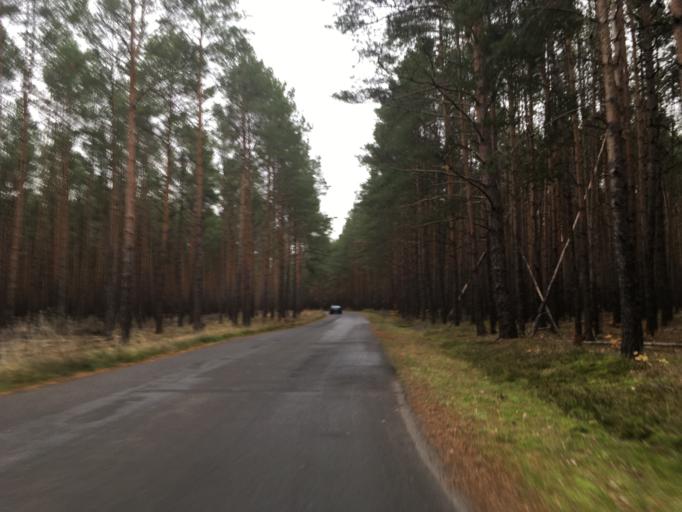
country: DE
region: Brandenburg
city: Mullrose
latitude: 52.2620
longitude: 14.4761
